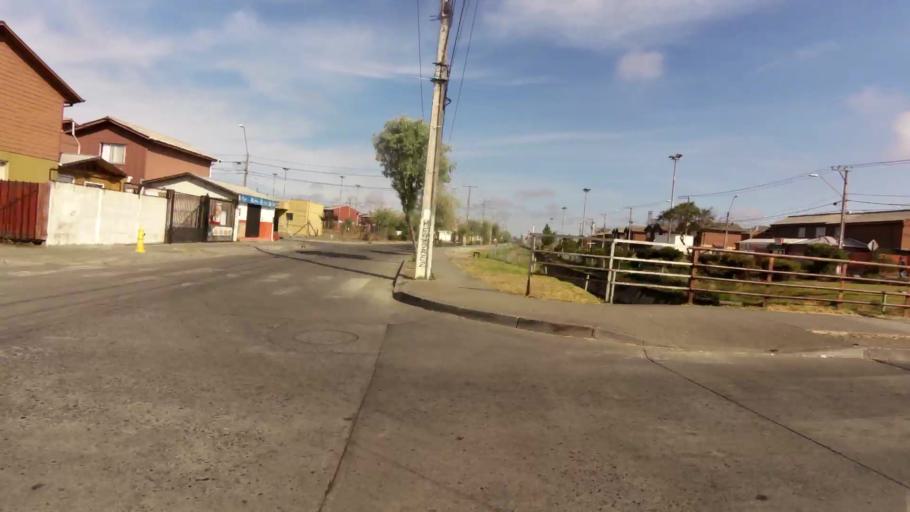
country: CL
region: Biobio
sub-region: Provincia de Concepcion
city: Talcahuano
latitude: -36.7938
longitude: -73.1148
